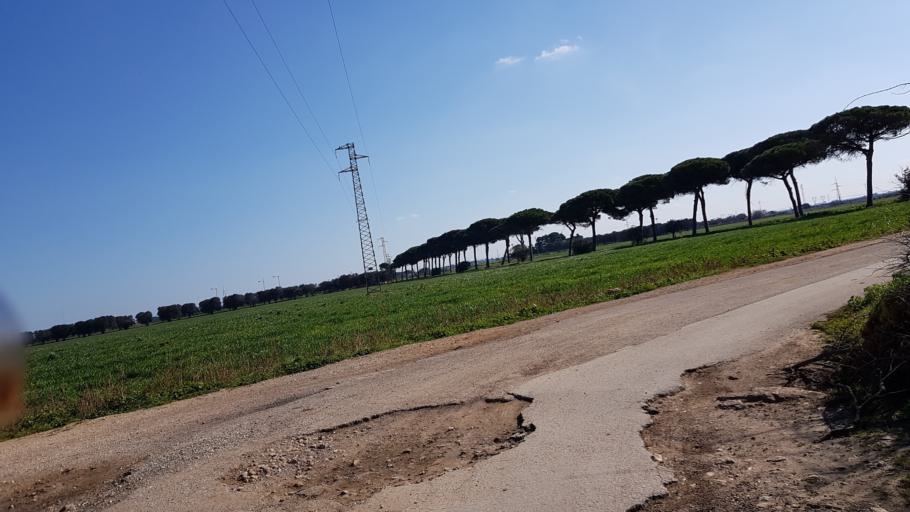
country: IT
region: Apulia
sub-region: Provincia di Brindisi
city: Mesagne
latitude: 40.6207
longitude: 17.8519
